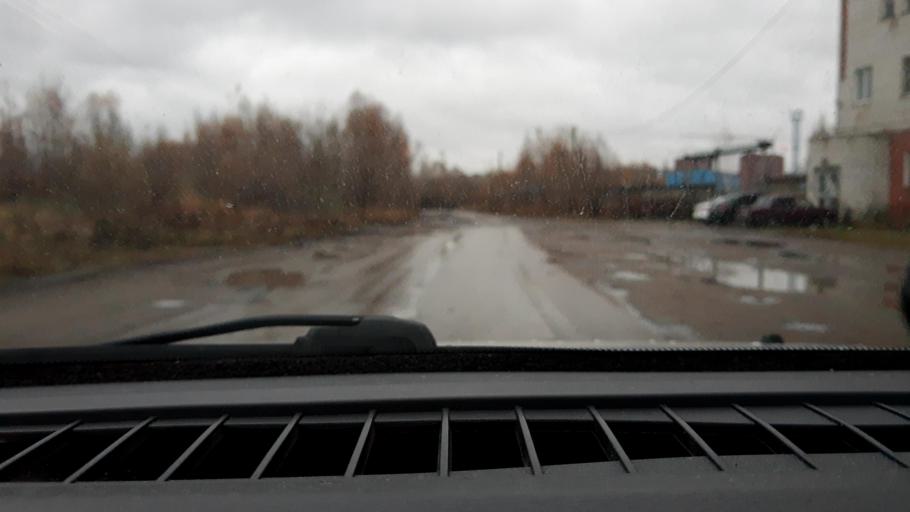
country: RU
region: Nizjnij Novgorod
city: Gorbatovka
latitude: 56.2707
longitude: 43.8535
